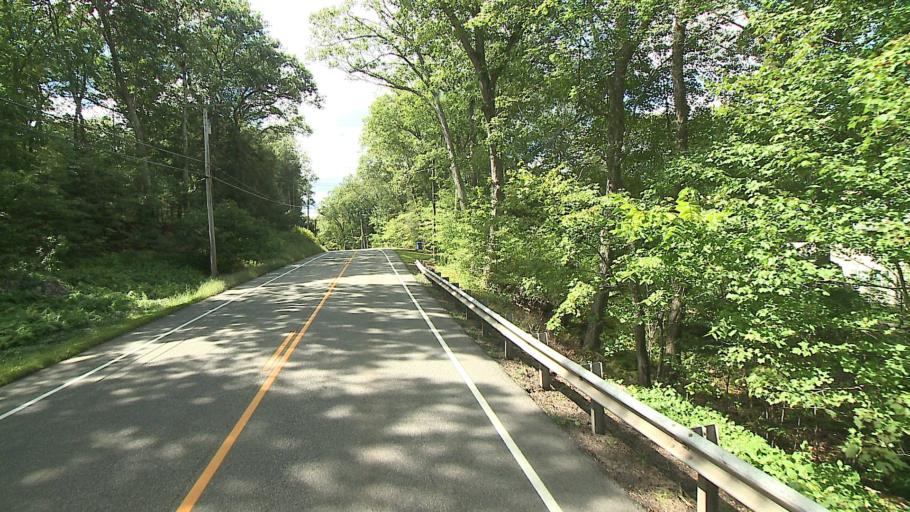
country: US
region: Connecticut
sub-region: Tolland County
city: Storrs
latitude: 41.8221
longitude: -72.2814
